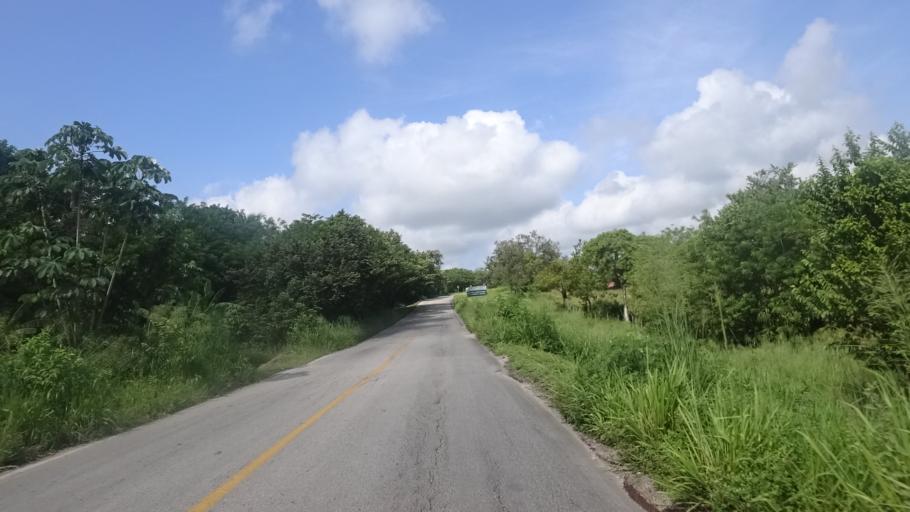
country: MX
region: Chiapas
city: Palenque
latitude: 17.5521
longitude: -91.9979
